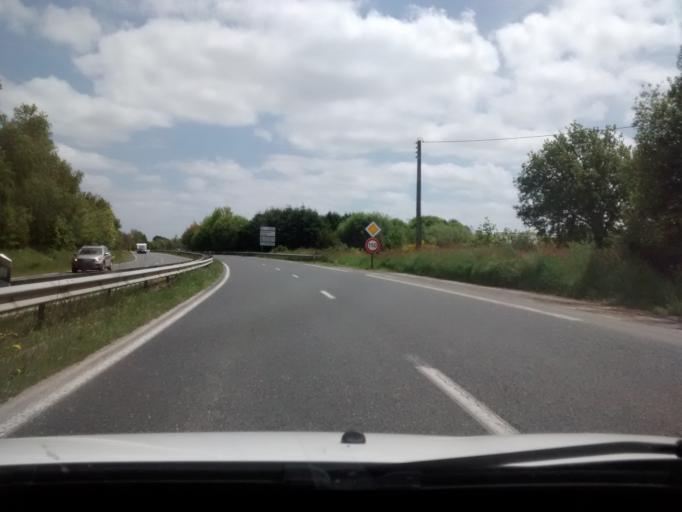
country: FR
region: Brittany
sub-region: Departement des Cotes-d'Armor
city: Cavan
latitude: 48.6550
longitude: -3.3350
